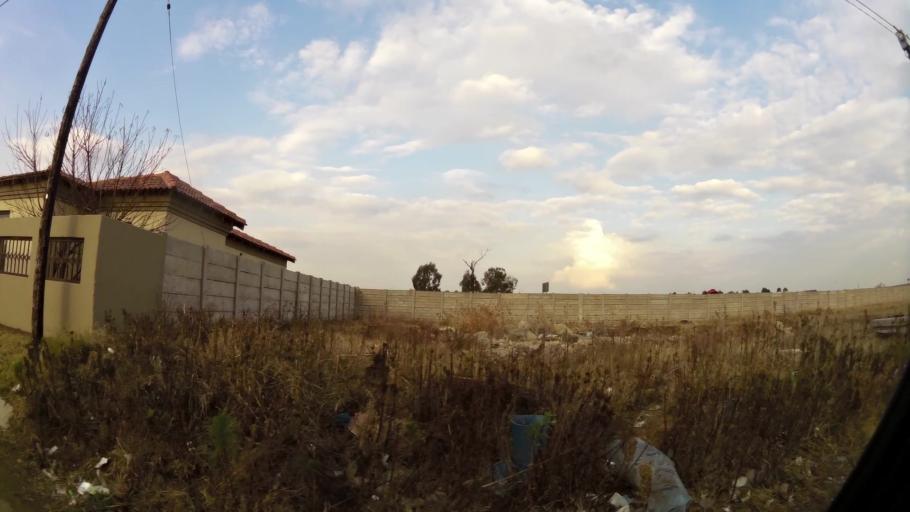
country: ZA
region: Gauteng
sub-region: Sedibeng District Municipality
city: Vanderbijlpark
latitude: -26.6132
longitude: 27.8138
